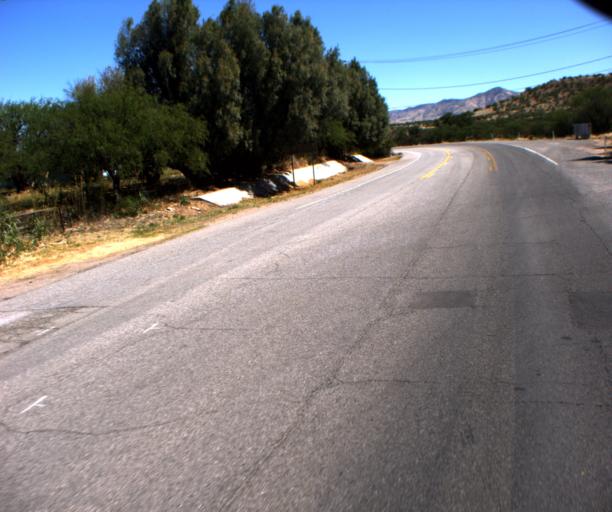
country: US
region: Arizona
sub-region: Santa Cruz County
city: Nogales
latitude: 31.3884
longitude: -110.8724
